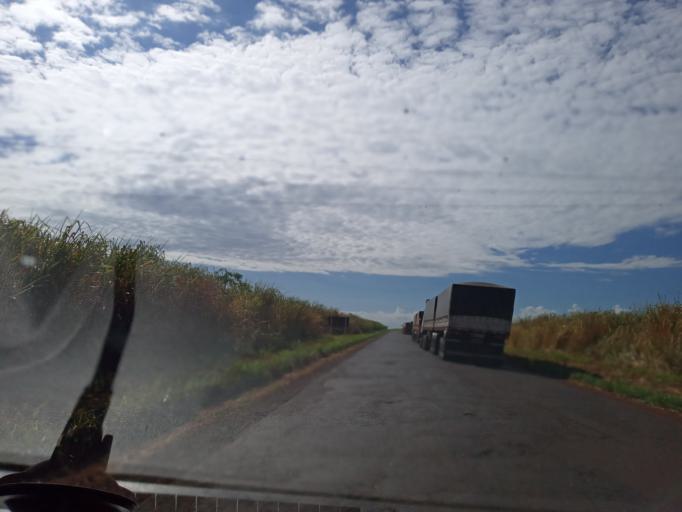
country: BR
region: Goias
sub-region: Itumbiara
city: Itumbiara
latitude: -18.4635
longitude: -49.1320
